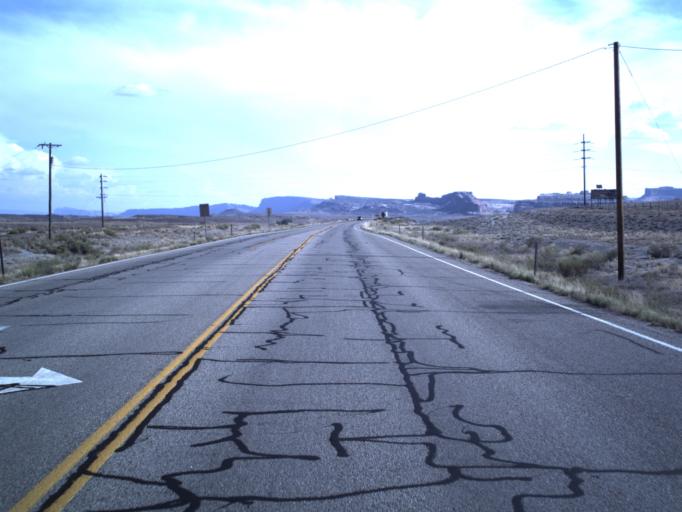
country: US
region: Utah
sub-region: Grand County
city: Moab
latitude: 38.7615
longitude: -109.7425
